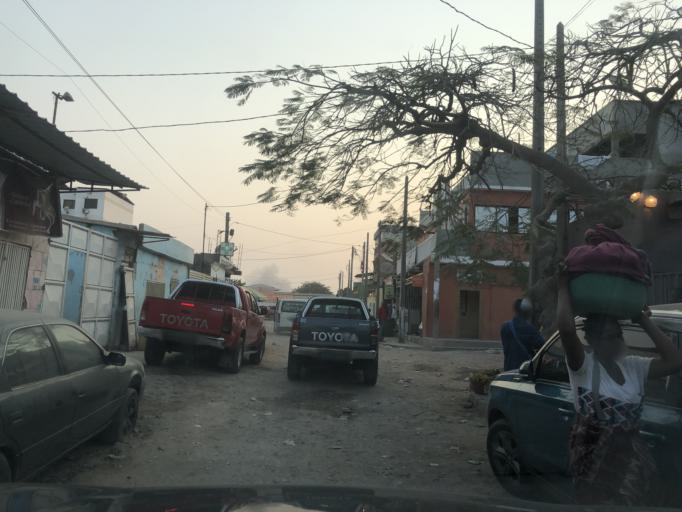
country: AO
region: Luanda
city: Luanda
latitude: -8.8478
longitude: 13.2272
